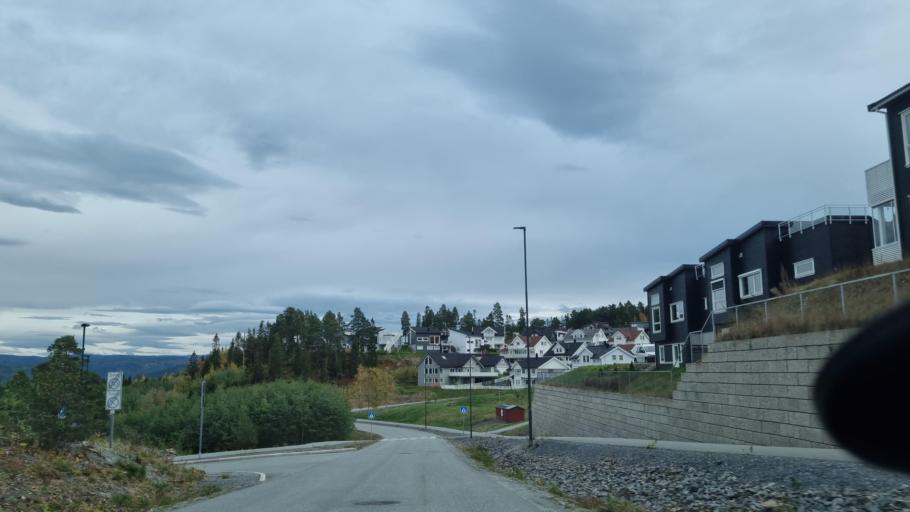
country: NO
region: Sor-Trondelag
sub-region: Malvik
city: Hommelvik
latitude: 63.4267
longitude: 10.7579
